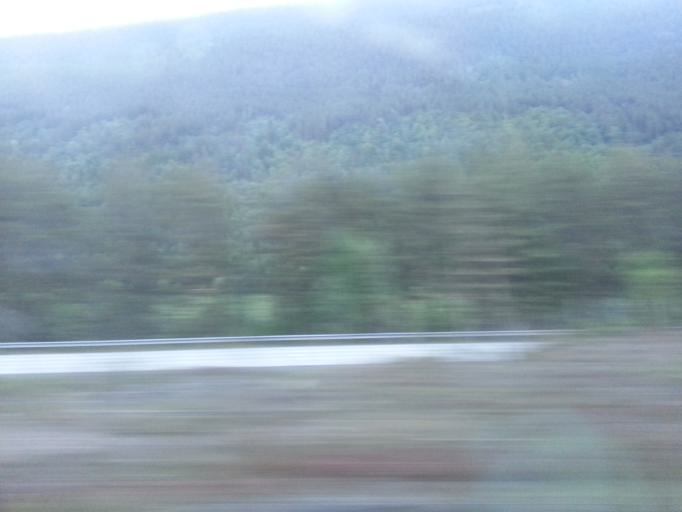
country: NO
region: Oppland
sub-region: Dovre
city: Dovre
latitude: 61.9456
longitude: 9.2981
